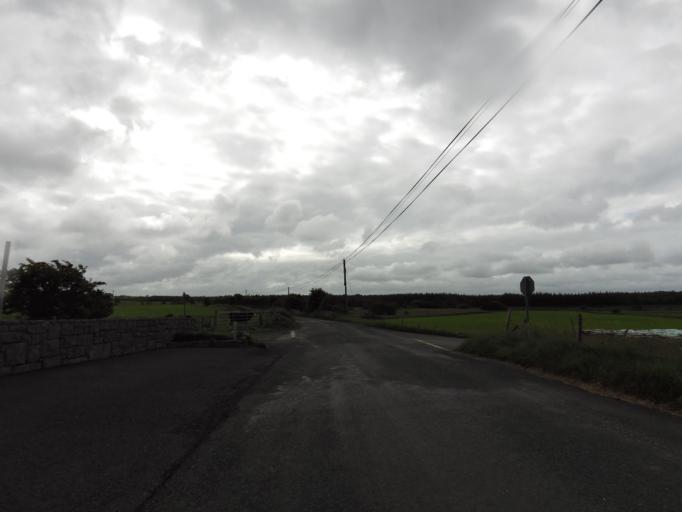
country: IE
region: Connaught
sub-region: County Galway
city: Athenry
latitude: 53.2916
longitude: -8.7025
